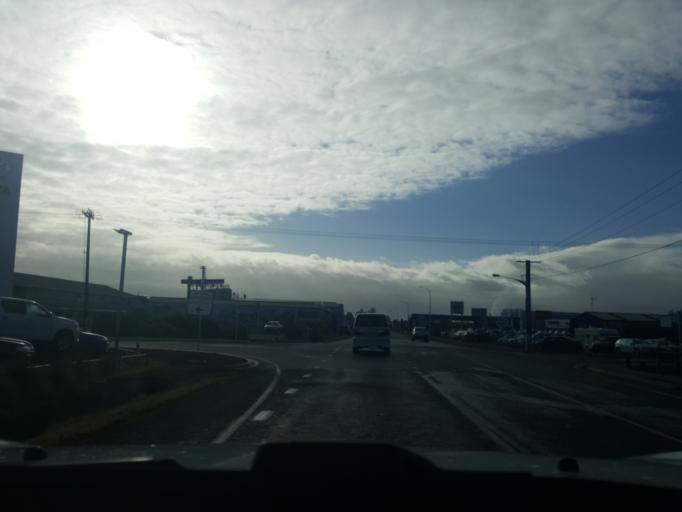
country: NZ
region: Waikato
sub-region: Waipa District
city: Cambridge
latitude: -37.6619
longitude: 175.5169
